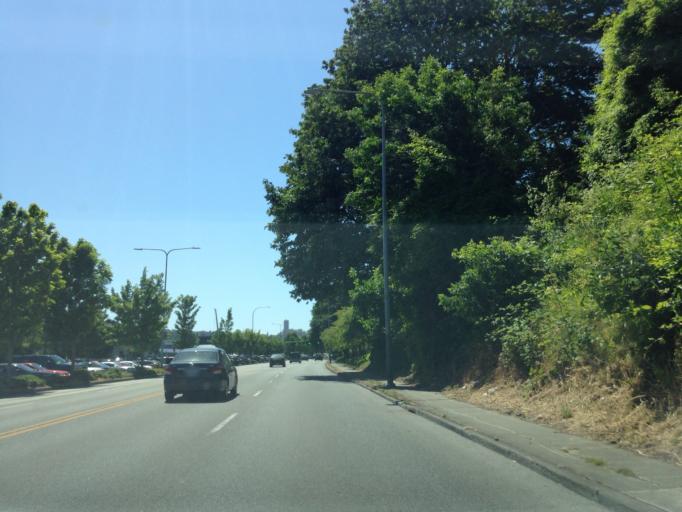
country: US
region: Washington
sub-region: King County
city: Seattle
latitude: 47.6399
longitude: -122.3420
